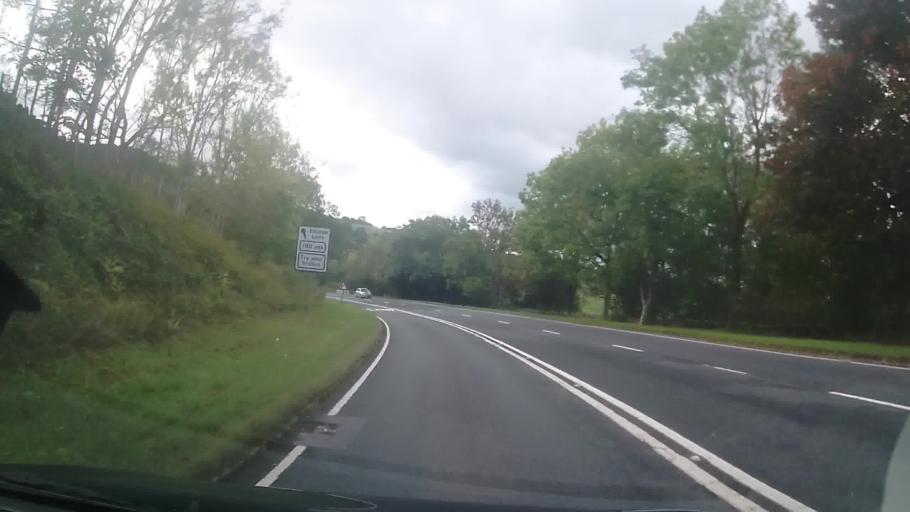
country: GB
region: England
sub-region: Worcestershire
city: Broadway
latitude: 52.0338
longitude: -1.8370
